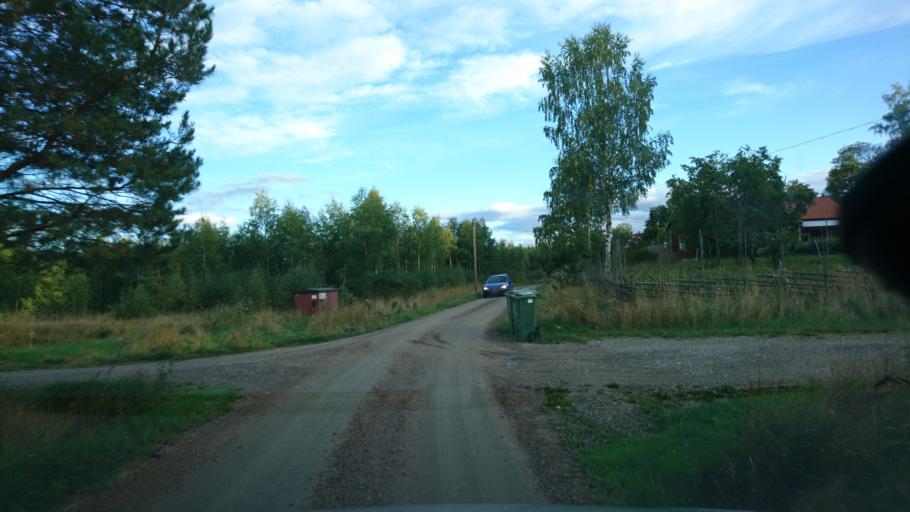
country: SE
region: Soedermanland
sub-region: Strangnas Kommun
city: Stallarholmen
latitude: 59.3731
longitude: 17.2280
